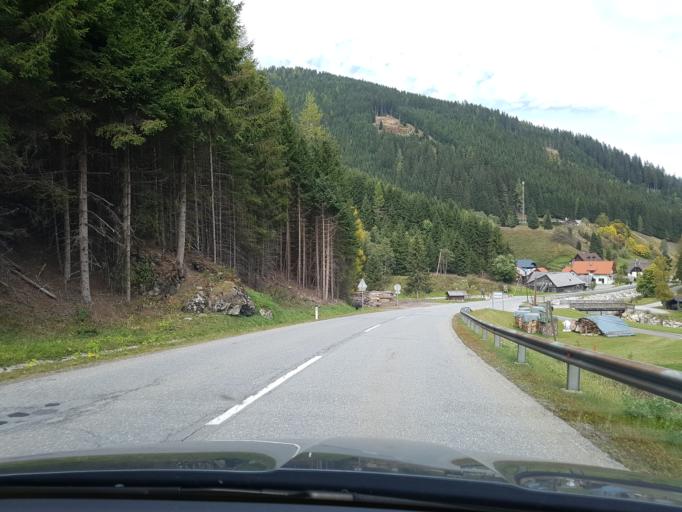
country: AT
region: Salzburg
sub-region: Politischer Bezirk Tamsweg
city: Ramingstein
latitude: 46.9587
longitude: 13.8822
